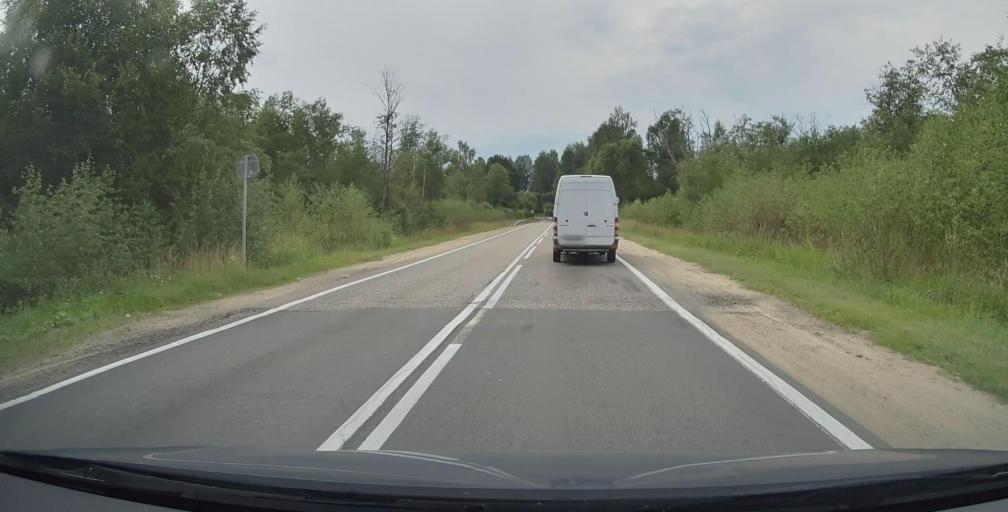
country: RU
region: Jaroslavl
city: Rybinsk
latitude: 57.9772
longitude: 38.7439
